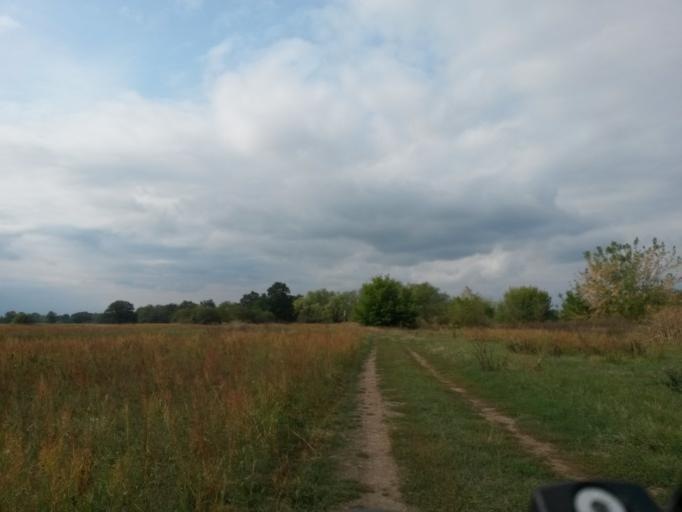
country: DE
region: Saxony-Anhalt
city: Tangermunde
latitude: 52.5248
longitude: 11.9669
